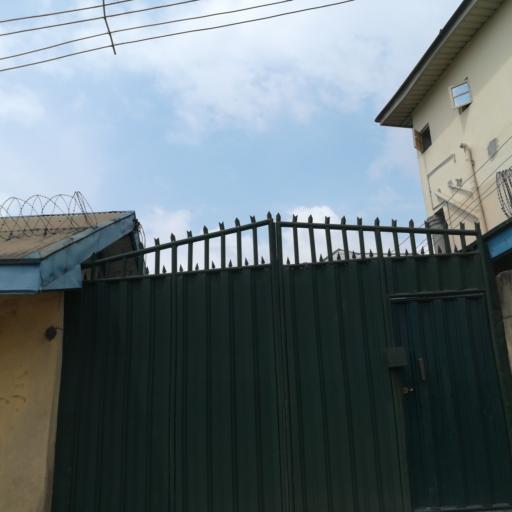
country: NG
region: Rivers
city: Port Harcourt
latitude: 4.8374
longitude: 7.0764
